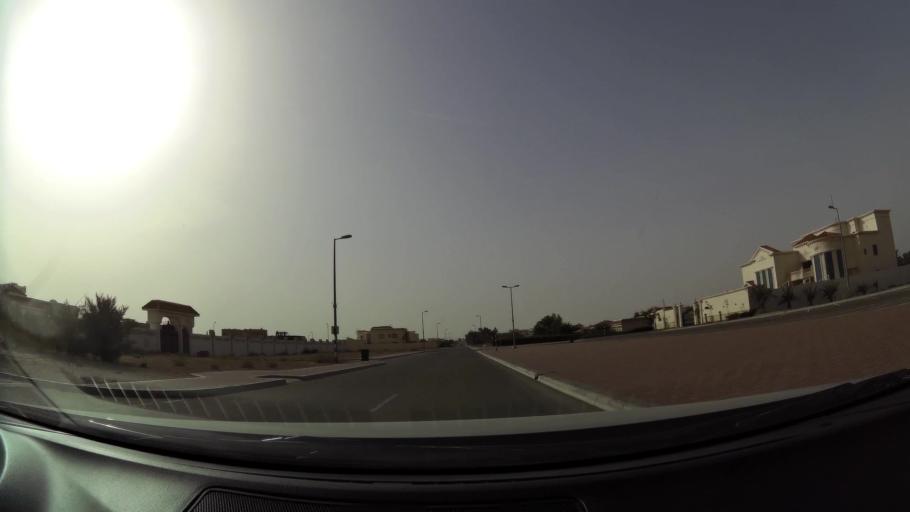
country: AE
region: Abu Dhabi
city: Al Ain
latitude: 24.1974
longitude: 55.6167
